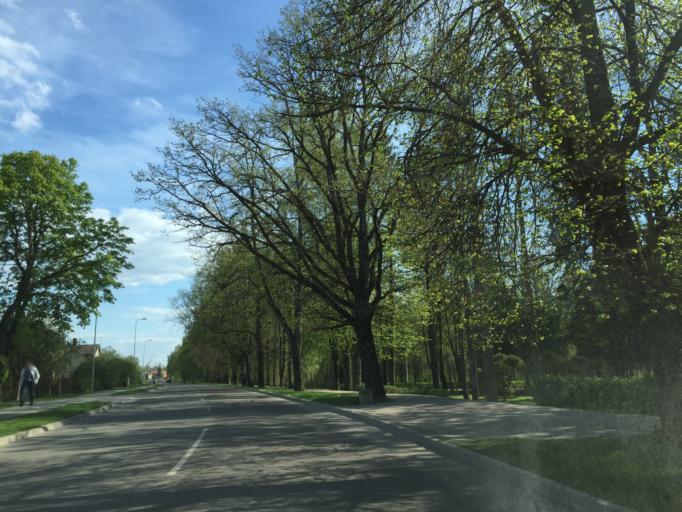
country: LV
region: Limbazu Rajons
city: Limbazi
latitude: 57.5076
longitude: 24.7137
